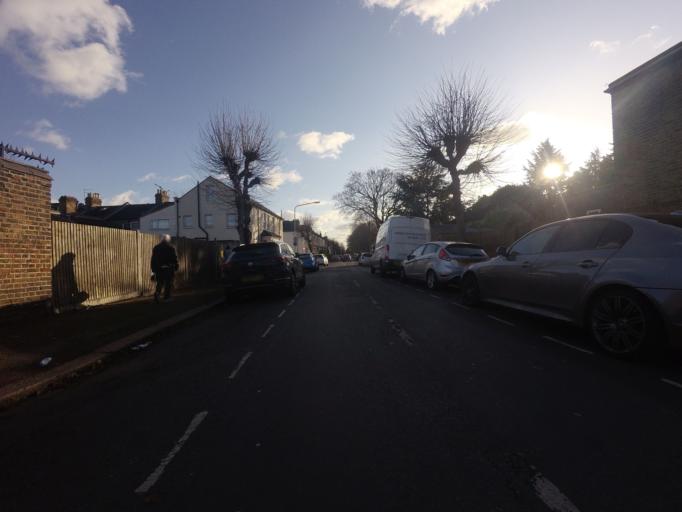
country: GB
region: England
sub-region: Greater London
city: East Ham
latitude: 51.5432
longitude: 0.0469
